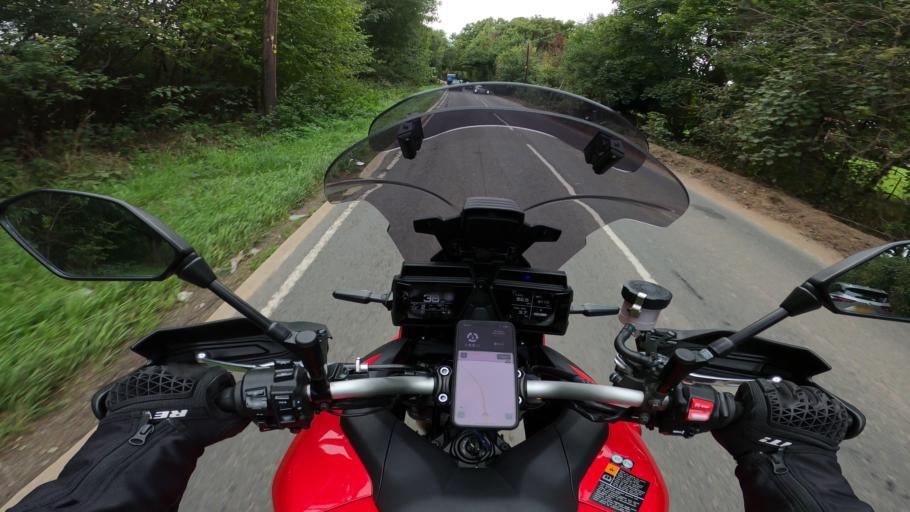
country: GB
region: England
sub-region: West Sussex
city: Crawley Down
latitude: 51.1515
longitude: -0.0822
